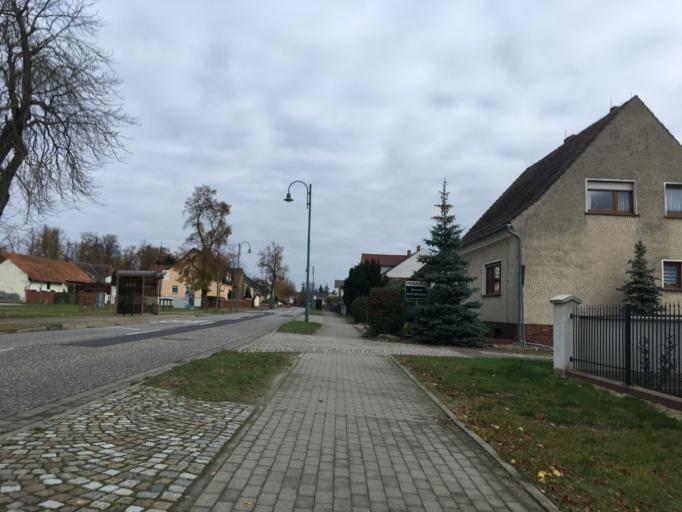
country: DE
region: Brandenburg
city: Tauer
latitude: 51.8954
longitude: 14.4522
